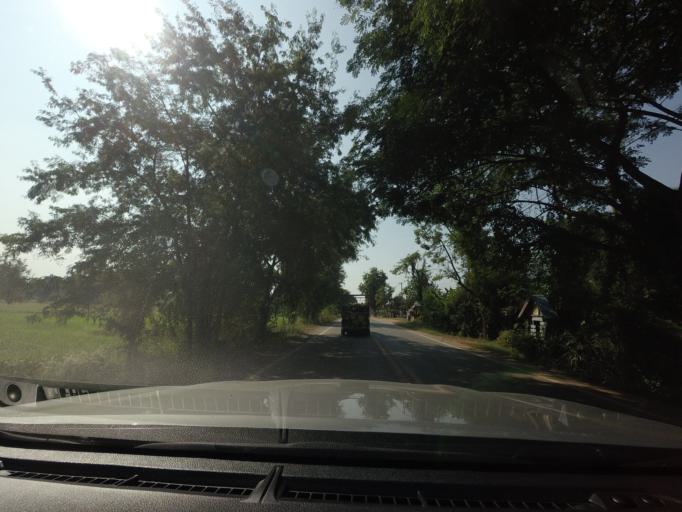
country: TH
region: Sukhothai
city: Kong Krailat
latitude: 16.8545
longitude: 99.9401
